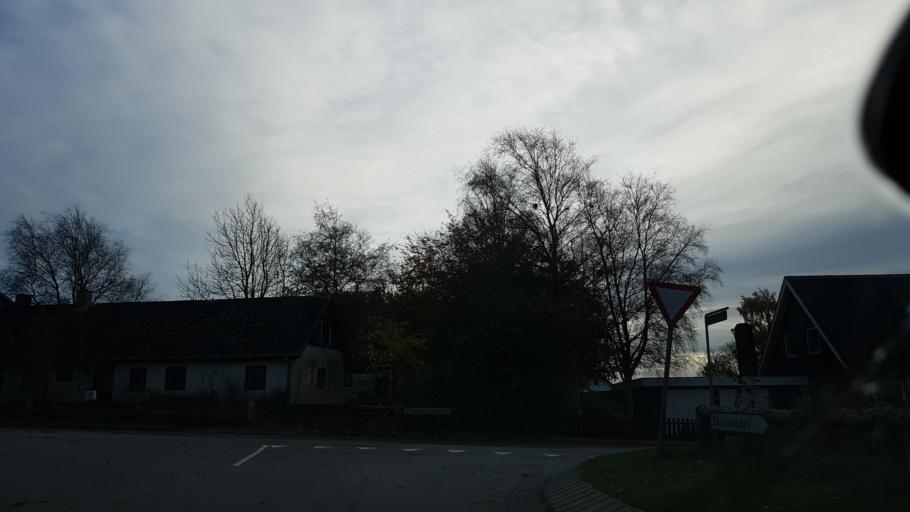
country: DK
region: South Denmark
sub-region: Haderslev Kommune
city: Vojens
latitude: 55.3013
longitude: 9.3773
